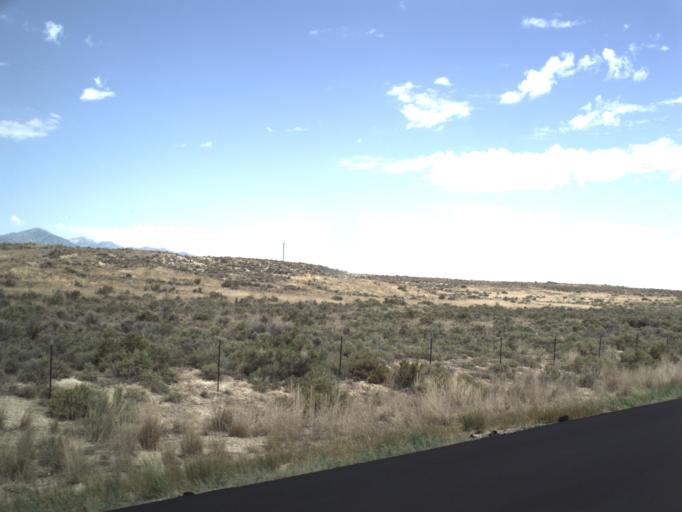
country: US
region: Utah
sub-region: Tooele County
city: Tooele
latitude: 40.1891
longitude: -112.4178
